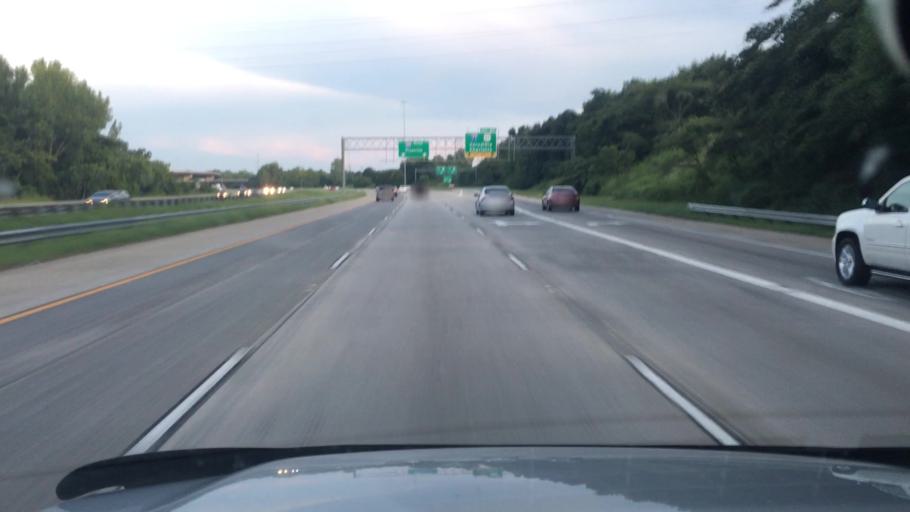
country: US
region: North Carolina
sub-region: Mecklenburg County
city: Pineville
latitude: 35.1314
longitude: -80.9234
